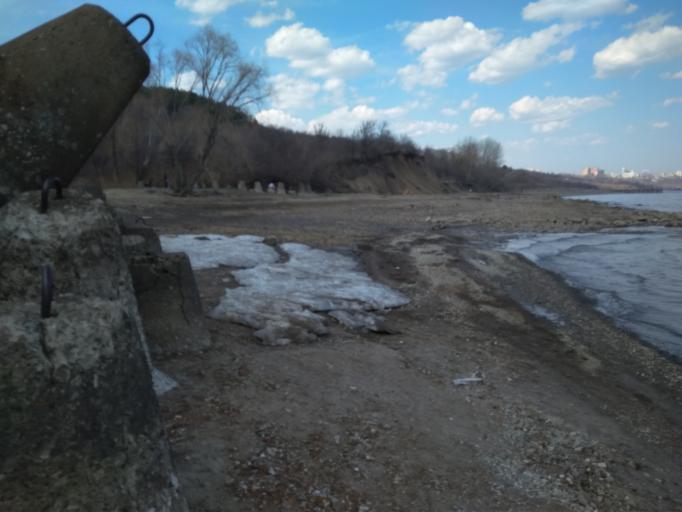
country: RU
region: Ulyanovsk
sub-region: Ulyanovskiy Rayon
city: Ulyanovsk
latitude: 54.2693
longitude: 48.3587
